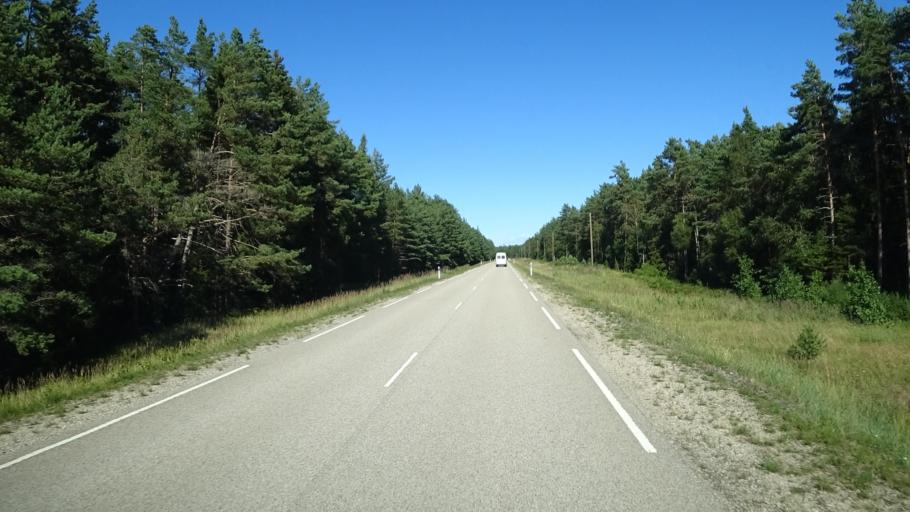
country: LV
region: Dundaga
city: Dundaga
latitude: 57.7316
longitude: 22.5133
